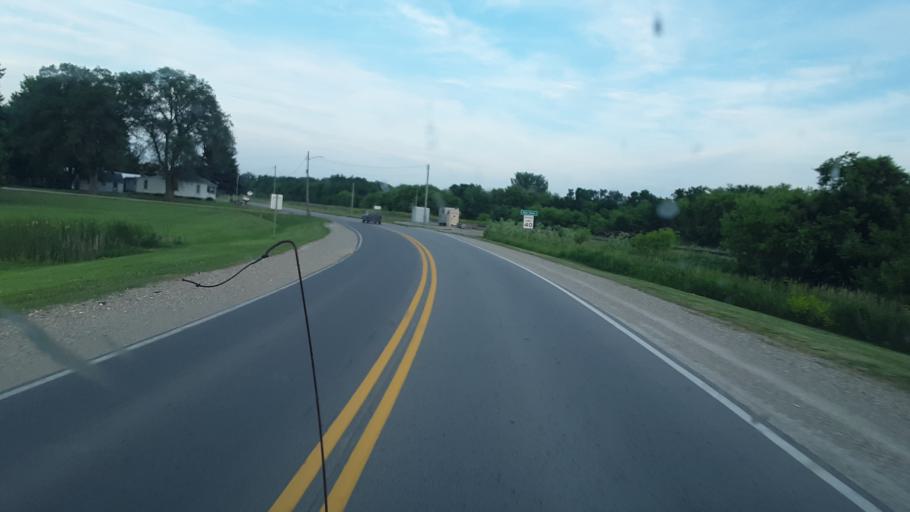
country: US
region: Iowa
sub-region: Benton County
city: Belle Plaine
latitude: 41.8978
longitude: -92.2895
